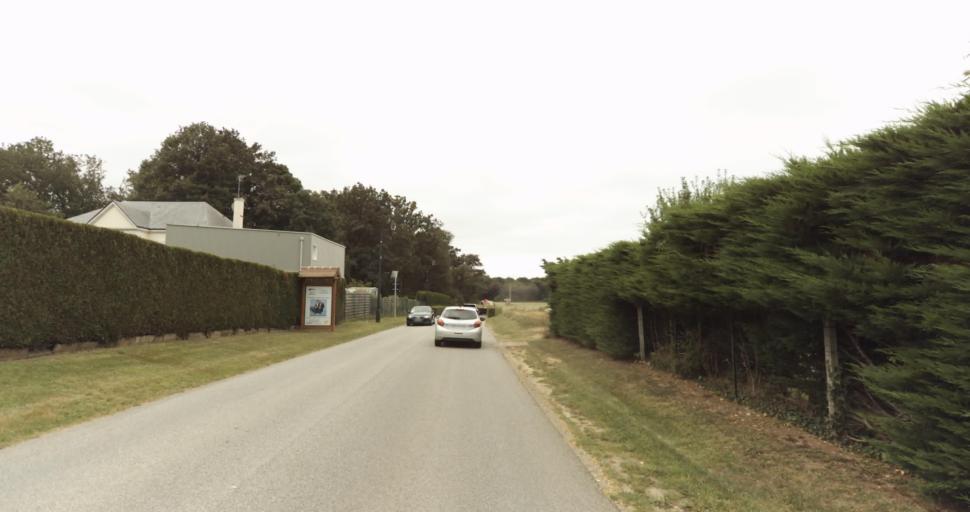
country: FR
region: Haute-Normandie
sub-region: Departement de l'Eure
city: Gravigny
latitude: 49.0350
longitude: 1.2023
